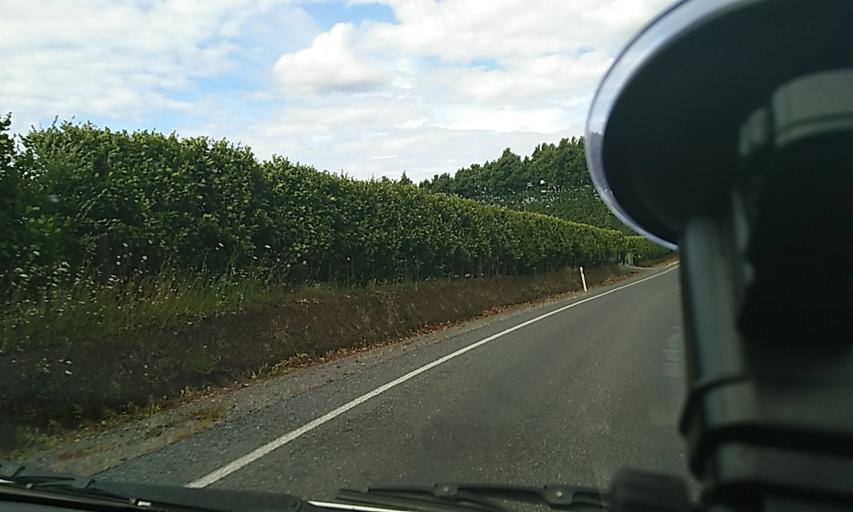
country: NZ
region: Bay of Plenty
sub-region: Western Bay of Plenty District
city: Waihi Beach
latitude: -37.4501
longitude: 175.9498
